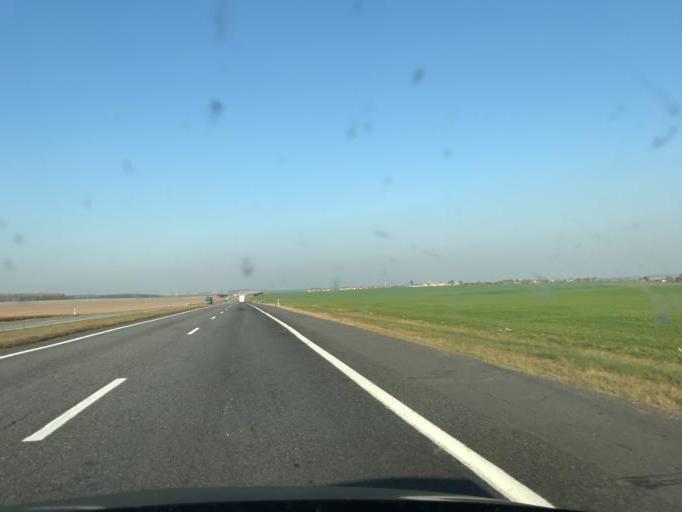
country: BY
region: Grodnenskaya
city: Mir
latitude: 53.4246
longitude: 26.5799
